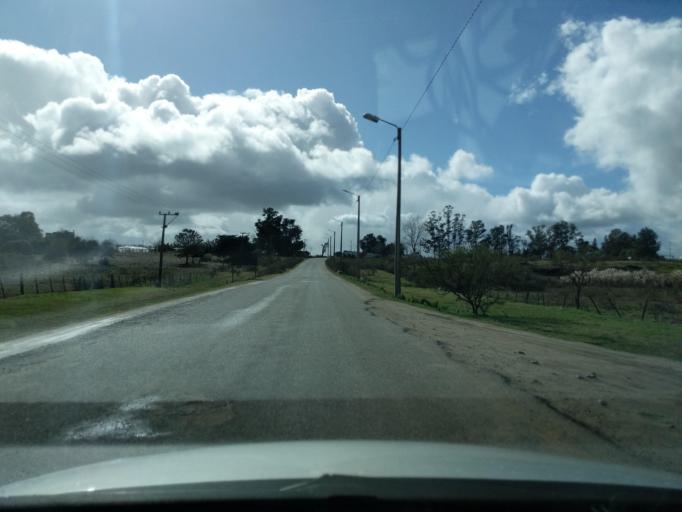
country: UY
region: Florida
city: Florida
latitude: -34.1117
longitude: -56.2265
